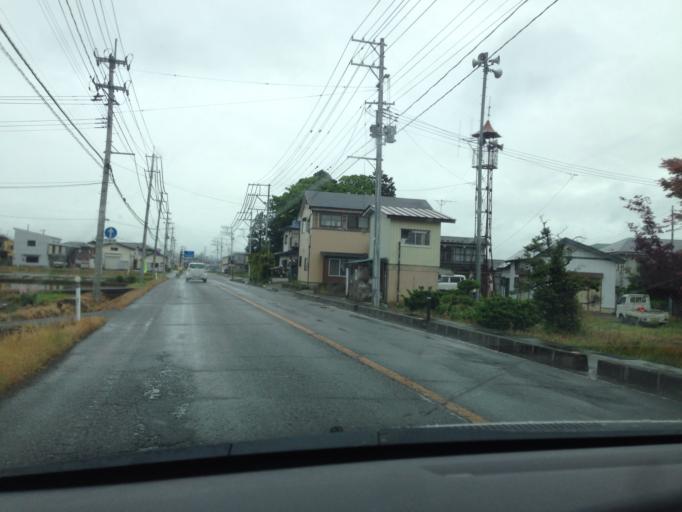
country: JP
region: Fukushima
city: Kitakata
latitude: 37.5538
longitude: 139.8302
